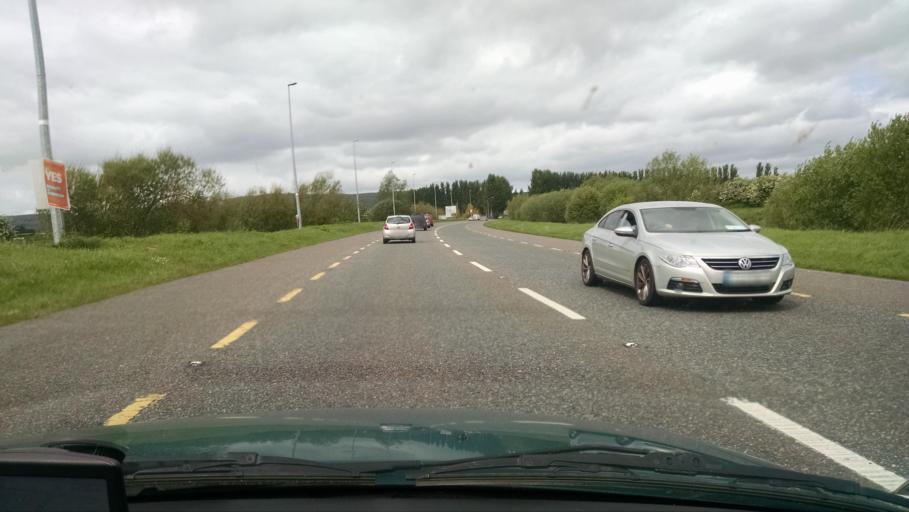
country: IE
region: Munster
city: Moyross
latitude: 52.6701
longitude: -8.6748
